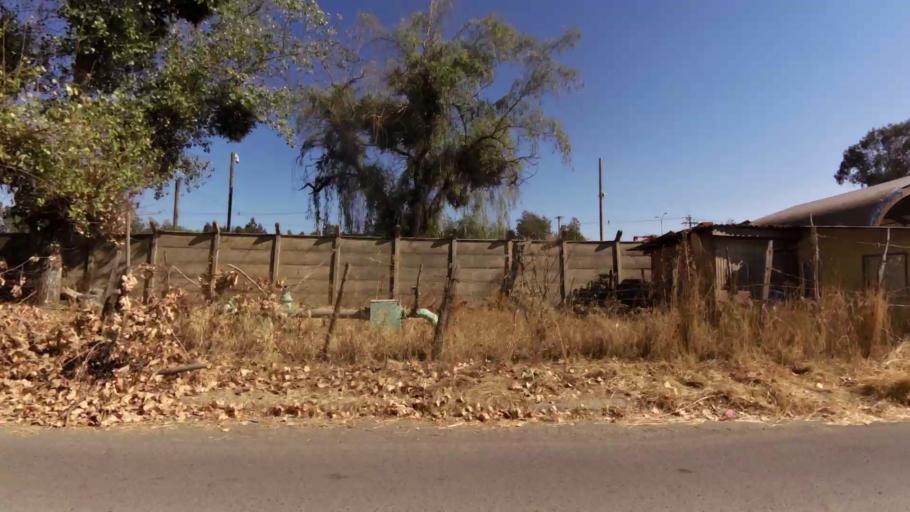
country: CL
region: Maule
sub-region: Provincia de Talca
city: Talca
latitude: -35.3987
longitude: -71.6225
